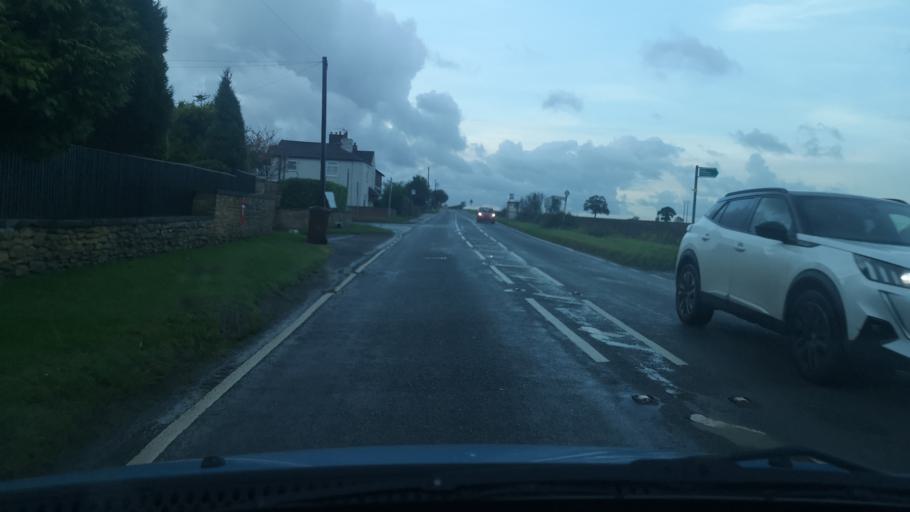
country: GB
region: England
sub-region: City and Borough of Wakefield
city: Badsworth
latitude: 53.6500
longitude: -1.2914
